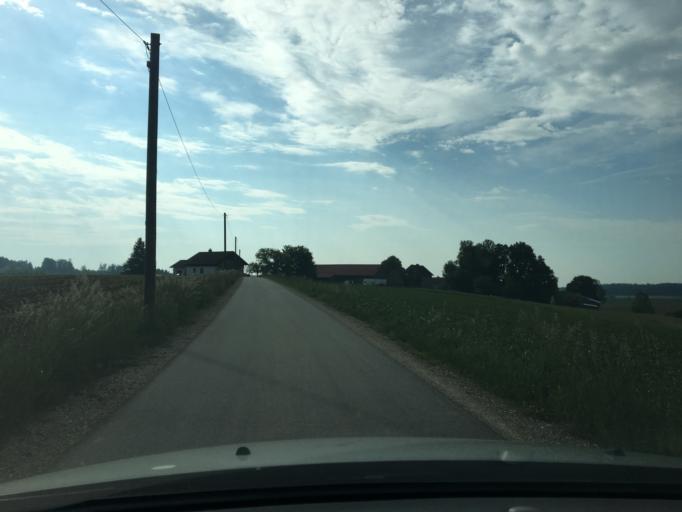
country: DE
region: Bavaria
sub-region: Upper Bavaria
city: Egglkofen
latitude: 48.4076
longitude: 12.4295
